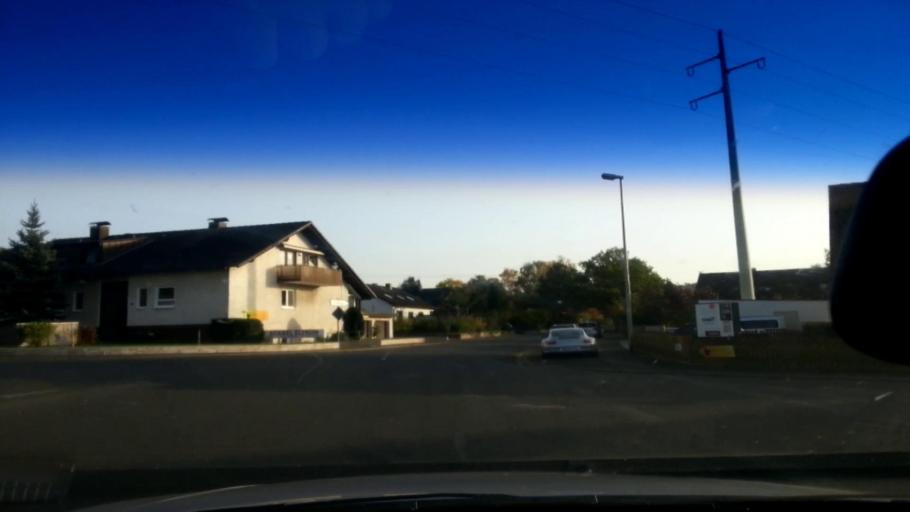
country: DE
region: Bavaria
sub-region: Upper Franconia
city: Zapfendorf
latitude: 50.0142
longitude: 10.9328
